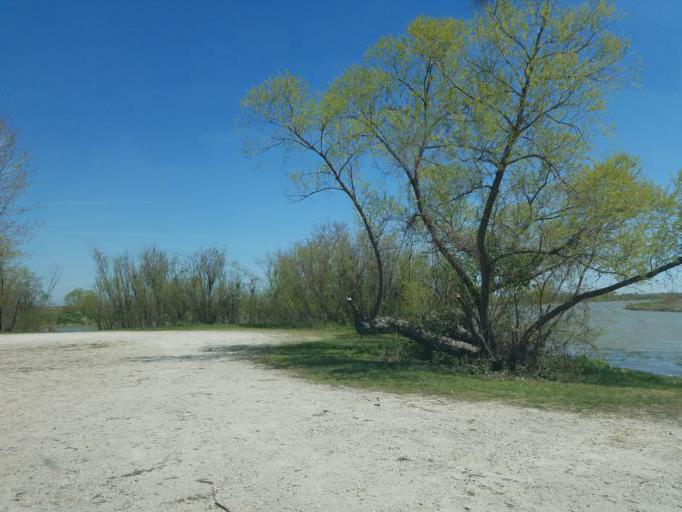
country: US
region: Ohio
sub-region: Ottawa County
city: Oak Harbor
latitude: 41.6044
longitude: -83.1534
